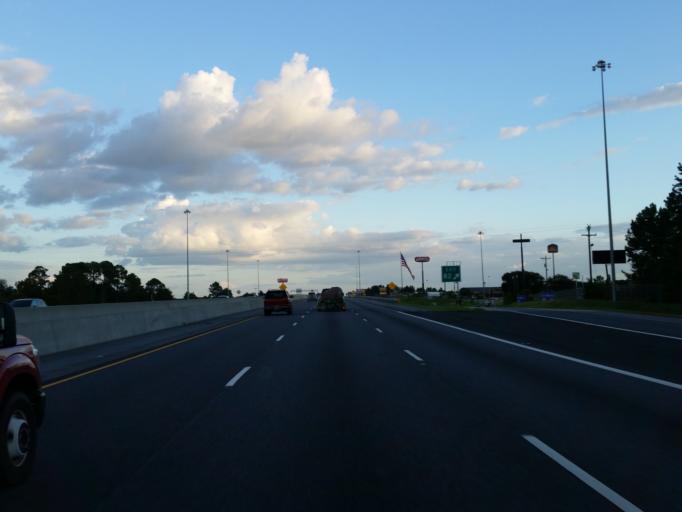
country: US
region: Georgia
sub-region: Turner County
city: Ashburn
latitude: 31.7142
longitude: -83.6383
